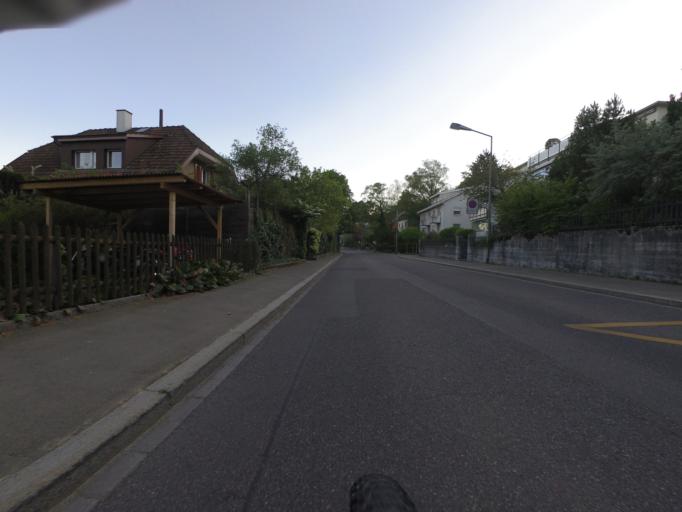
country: CH
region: Zurich
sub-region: Bezirk Winterthur
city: Oberwinterthur (Kreis 2) / Talacker
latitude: 47.5047
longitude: 8.7475
